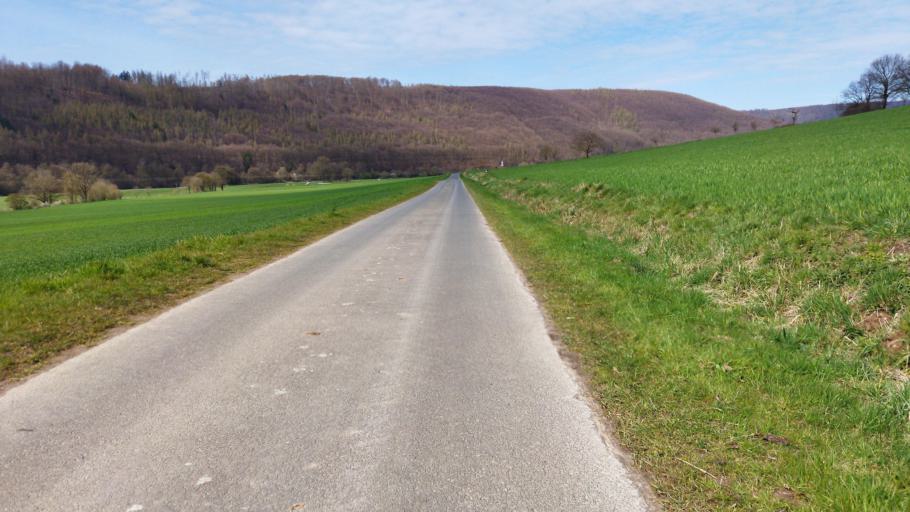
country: DE
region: Lower Saxony
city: Bad Karlshafen
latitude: 51.6324
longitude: 9.5026
